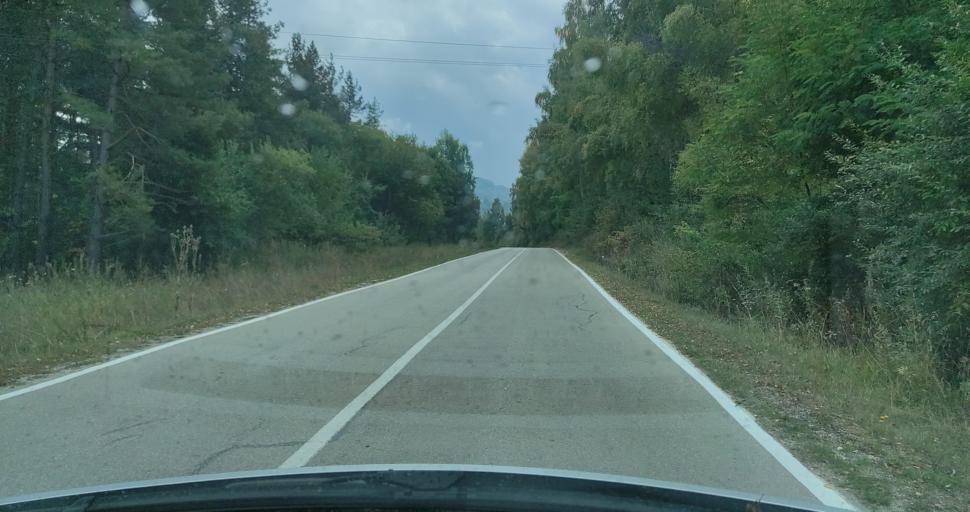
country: RS
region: Central Serbia
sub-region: Jablanicki Okrug
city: Crna Trava
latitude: 42.6740
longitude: 22.3148
